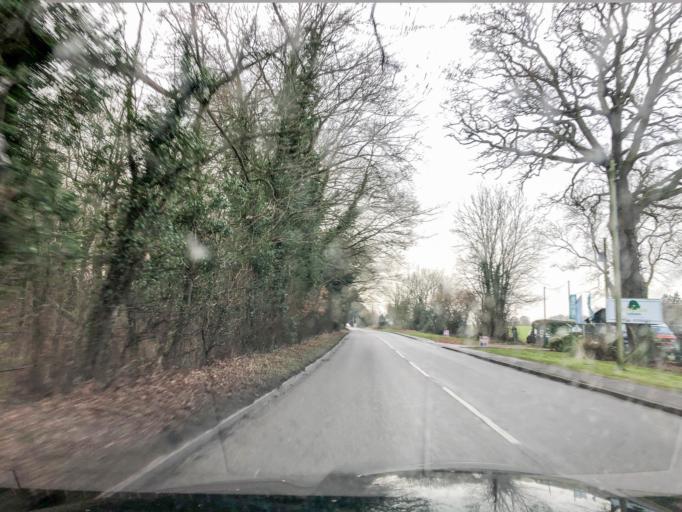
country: GB
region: England
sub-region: Warwickshire
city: Kenilworth
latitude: 52.3241
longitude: -1.5759
